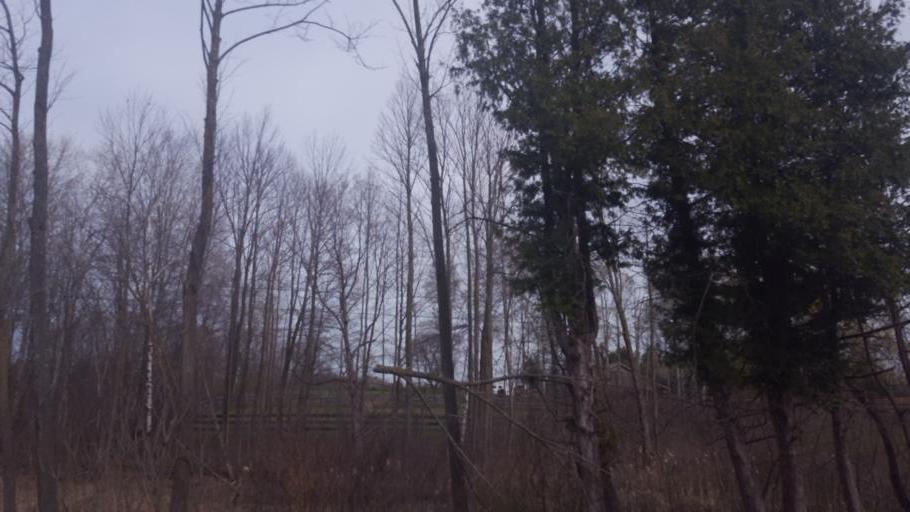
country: US
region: Michigan
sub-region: Clare County
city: Clare
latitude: 43.8686
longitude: -84.7680
